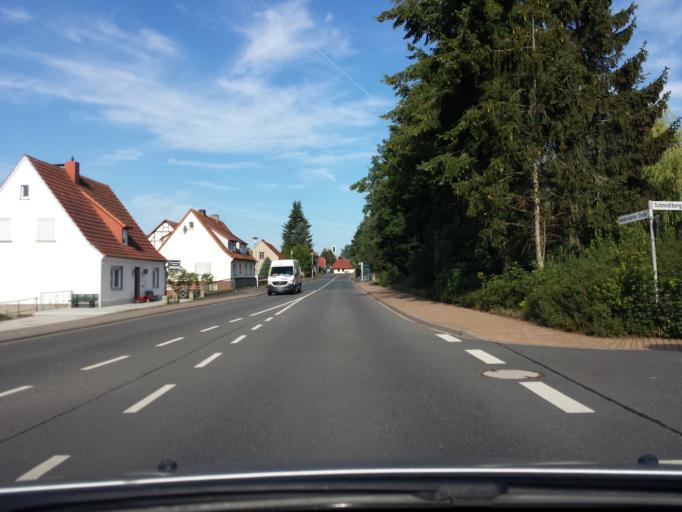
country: DE
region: Hesse
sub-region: Regierungsbezirk Kassel
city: Kirchheim
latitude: 50.8512
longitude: 9.5585
